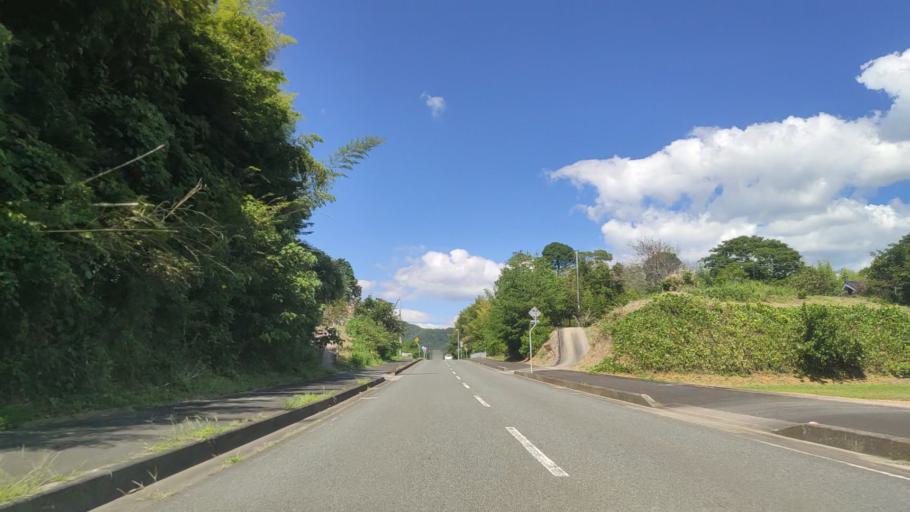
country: JP
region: Kyoto
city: Fukuchiyama
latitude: 35.2303
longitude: 135.1285
